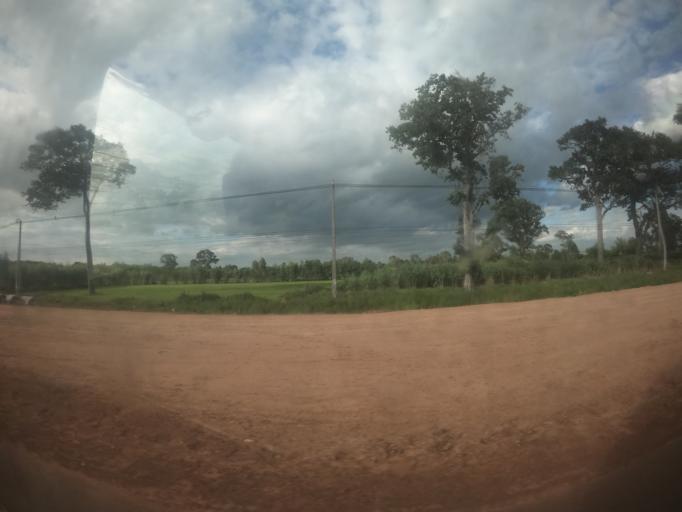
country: TH
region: Surin
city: Kap Choeng
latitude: 14.4930
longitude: 103.5716
